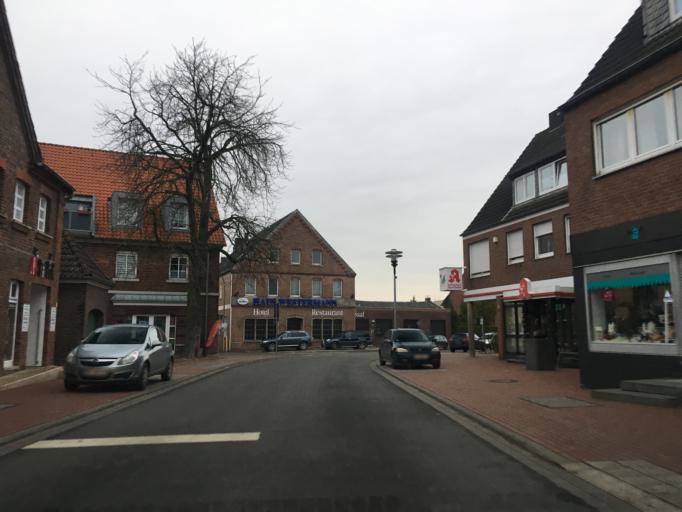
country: DE
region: North Rhine-Westphalia
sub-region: Regierungsbezirk Munster
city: Nordkirchen
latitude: 51.7380
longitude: 7.5255
